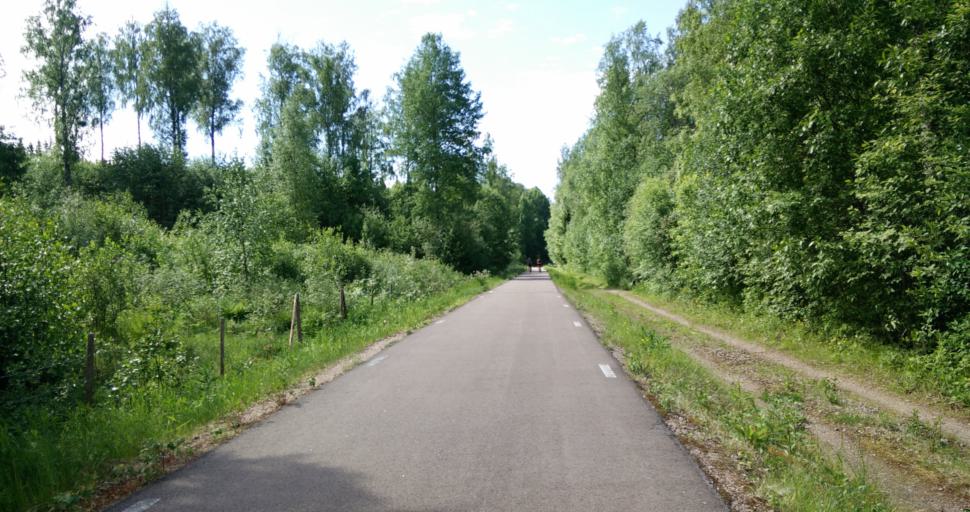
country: SE
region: Vaermland
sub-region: Hagfors Kommun
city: Hagfors
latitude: 59.9950
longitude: 13.5898
